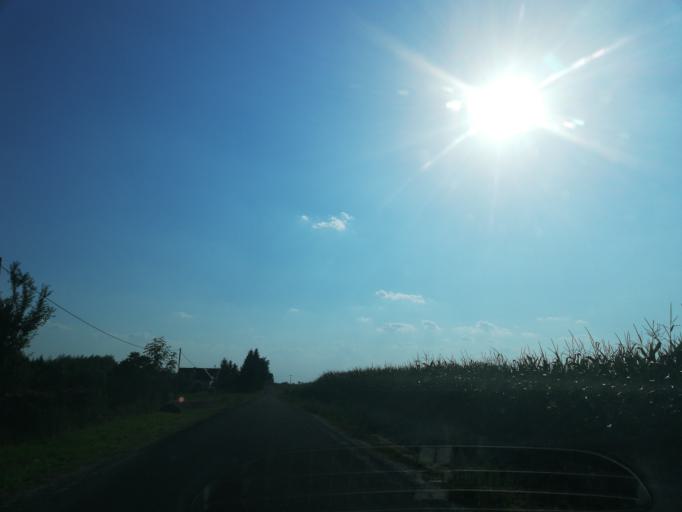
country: PL
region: Kujawsko-Pomorskie
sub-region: Powiat golubsko-dobrzynski
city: Kowalewo Pomorskie
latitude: 53.1066
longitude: 18.8975
